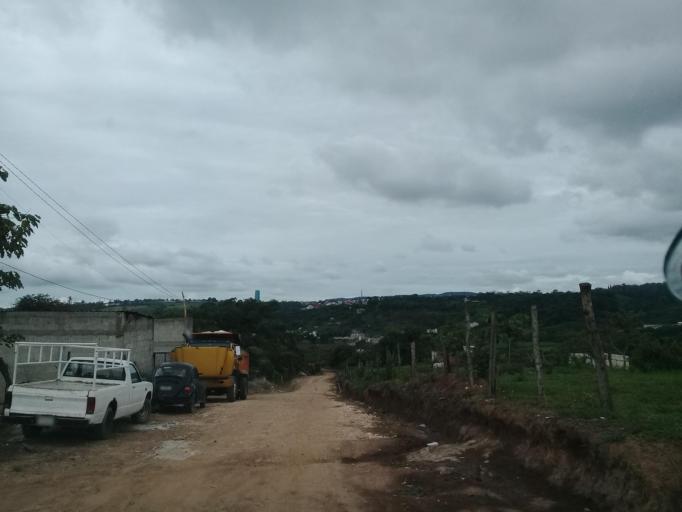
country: MX
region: Veracruz
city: El Castillo
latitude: 19.5524
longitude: -96.8764
